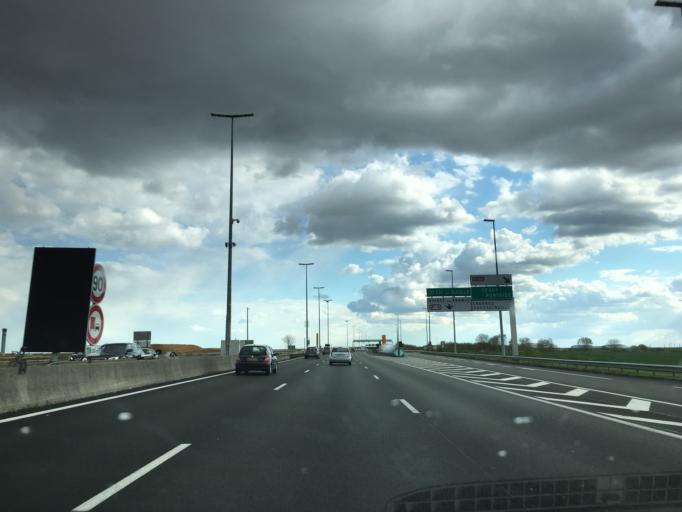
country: FR
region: Ile-de-France
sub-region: Departement du Val-d'Oise
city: Louvres
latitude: 49.0338
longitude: 2.5403
